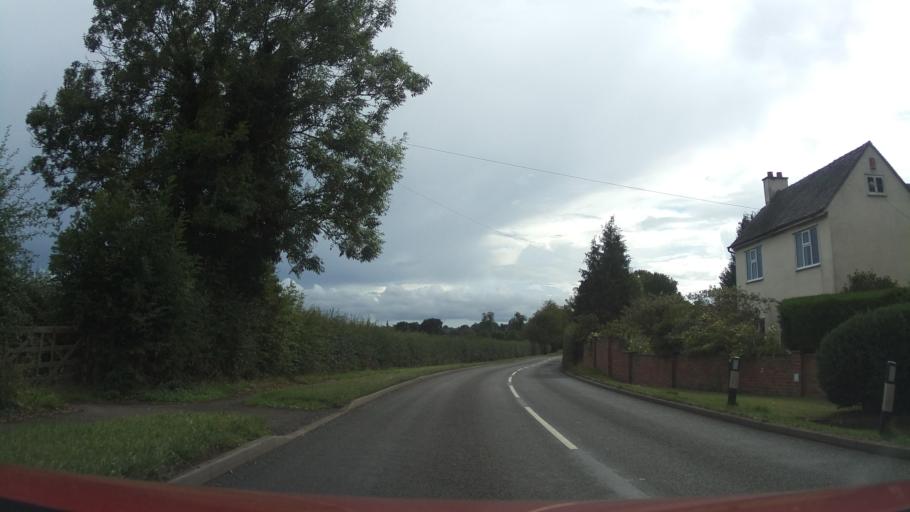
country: GB
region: England
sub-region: Staffordshire
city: Eccleshall
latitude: 52.8698
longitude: -2.2490
